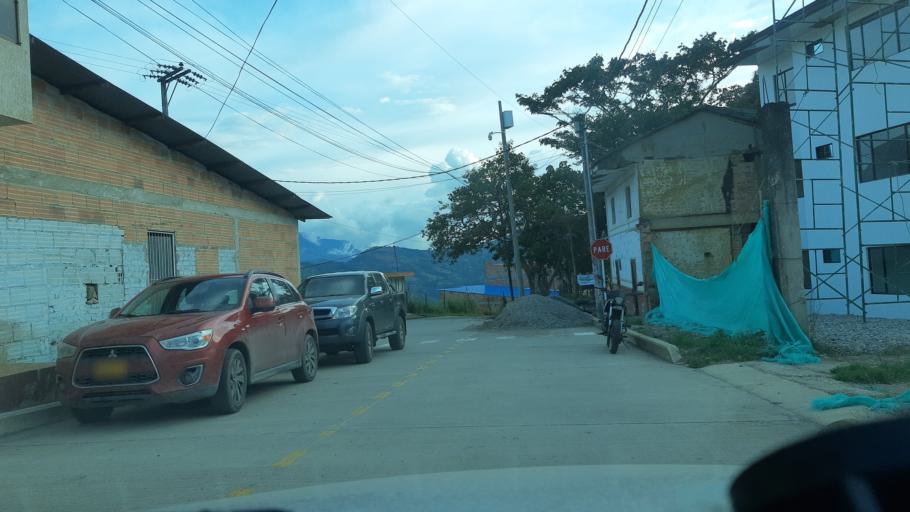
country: CO
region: Boyaca
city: Chivor
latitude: 4.9712
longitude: -73.3212
